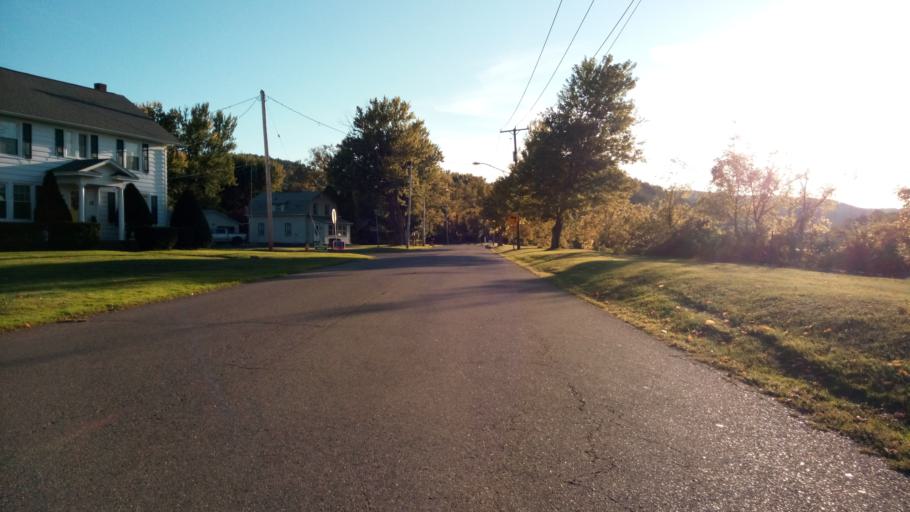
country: US
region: New York
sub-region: Chemung County
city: Elmira
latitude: 42.0787
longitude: -76.8213
